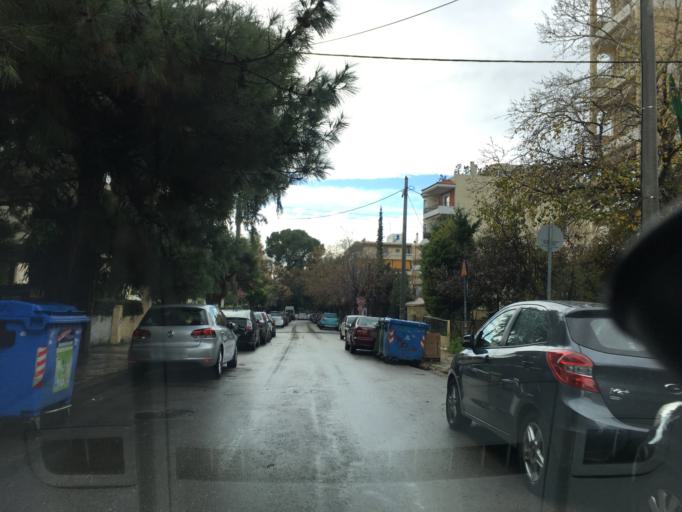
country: GR
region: Attica
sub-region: Nomarchia Athinas
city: Marousi
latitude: 38.0552
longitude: 23.8129
